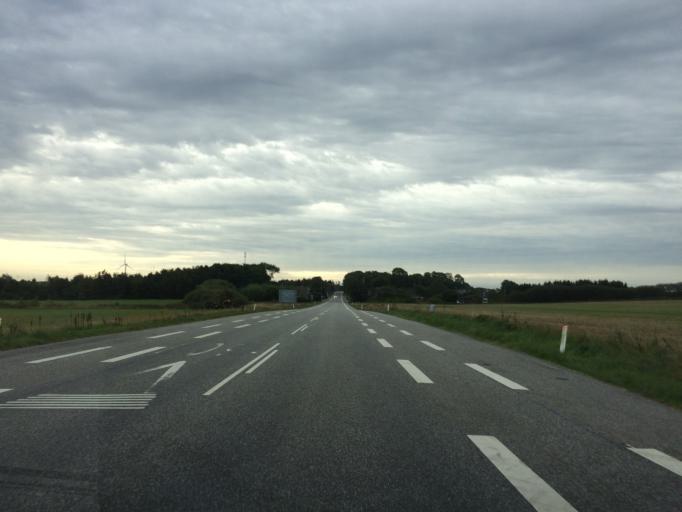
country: DK
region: South Denmark
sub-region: Vejle Kommune
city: Give
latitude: 55.7894
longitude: 9.1803
